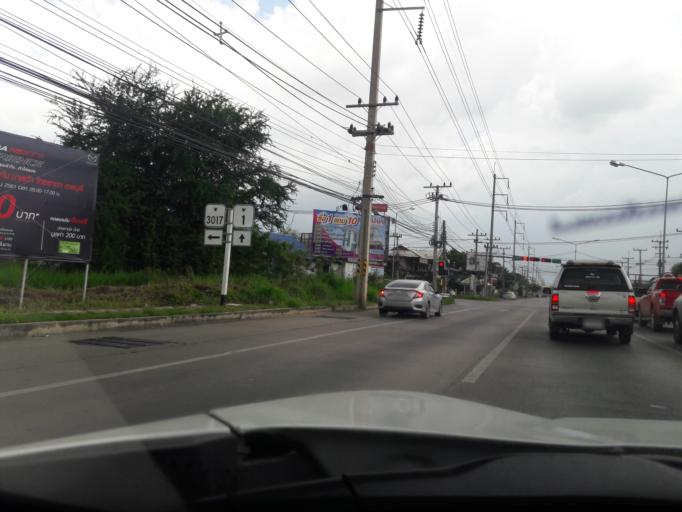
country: TH
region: Lop Buri
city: Lop Buri
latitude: 14.7803
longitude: 100.6887
